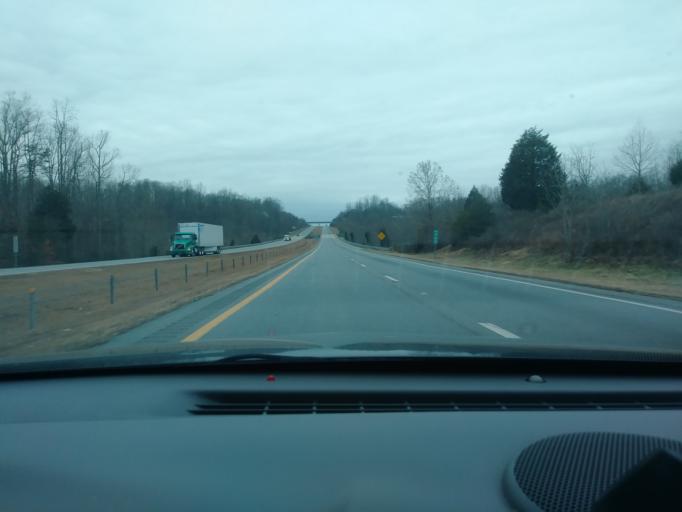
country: US
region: North Carolina
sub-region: Yadkin County
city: Yadkinville
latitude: 36.1187
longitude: -80.7184
